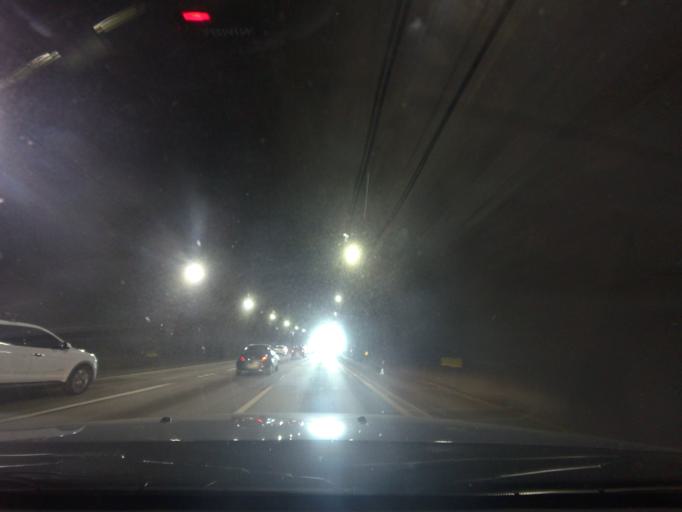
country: BR
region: Sao Paulo
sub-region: Cubatao
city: Cubatao
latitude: -23.9139
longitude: -46.5202
